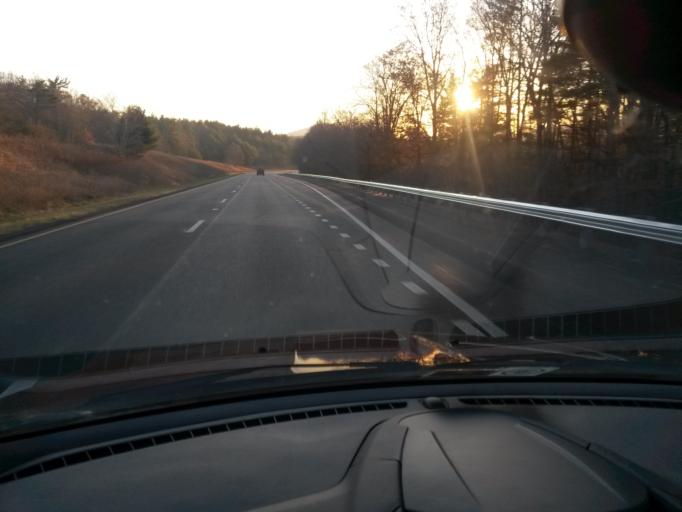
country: US
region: Virginia
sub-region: Alleghany County
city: Clifton Forge
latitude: 37.8178
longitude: -79.6678
